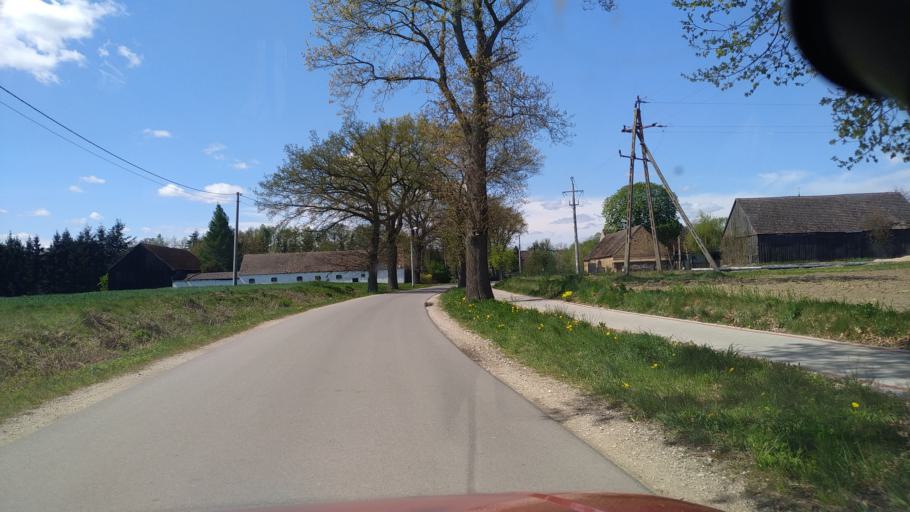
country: PL
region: Greater Poland Voivodeship
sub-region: Powiat zlotowski
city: Krajenka
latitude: 53.2659
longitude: 16.9049
